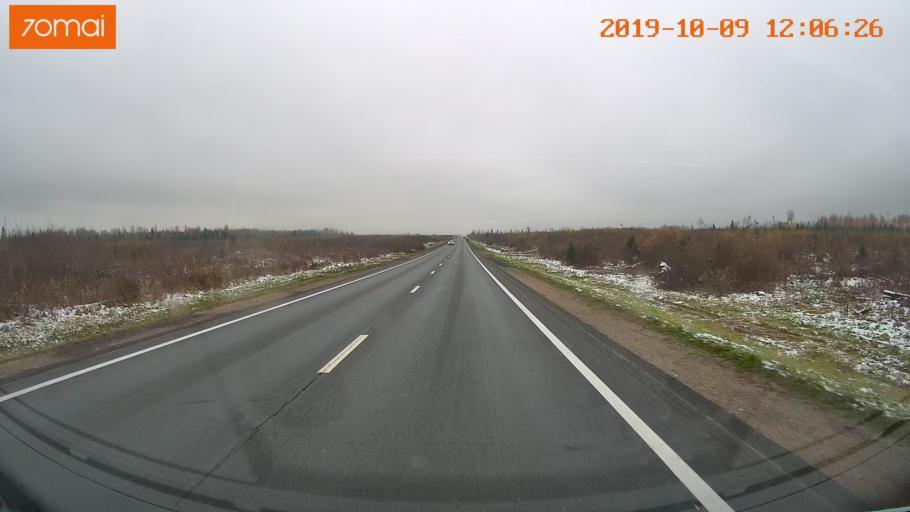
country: RU
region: Jaroslavl
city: Prechistoye
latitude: 58.6144
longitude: 40.3352
